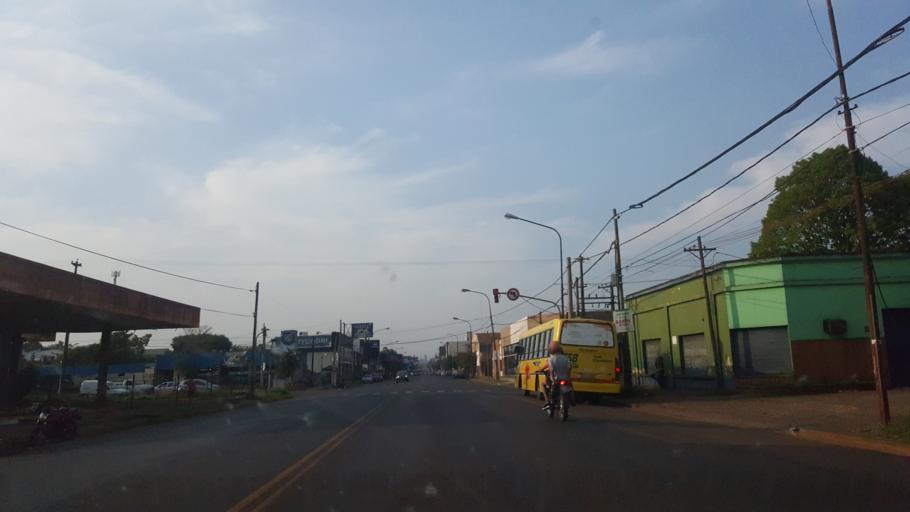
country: AR
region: Misiones
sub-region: Departamento de Capital
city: Posadas
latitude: -27.3983
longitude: -55.9019
